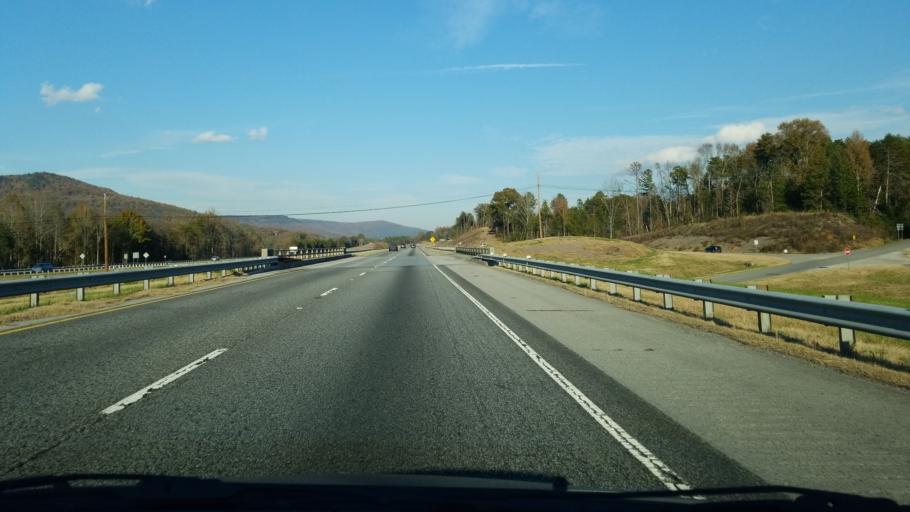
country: US
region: Georgia
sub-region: Dade County
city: Trenton
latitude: 34.9421
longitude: -85.4760
